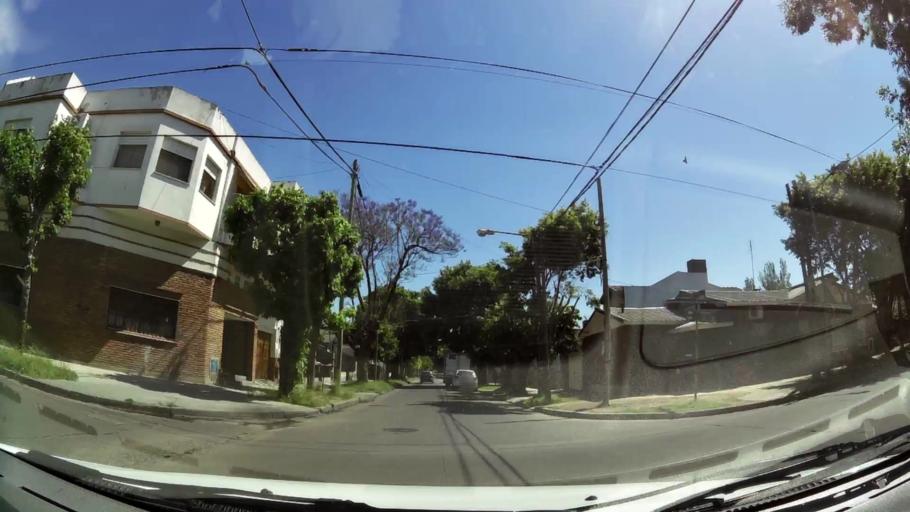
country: AR
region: Buenos Aires
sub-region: Partido de General San Martin
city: General San Martin
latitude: -34.5599
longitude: -58.5558
